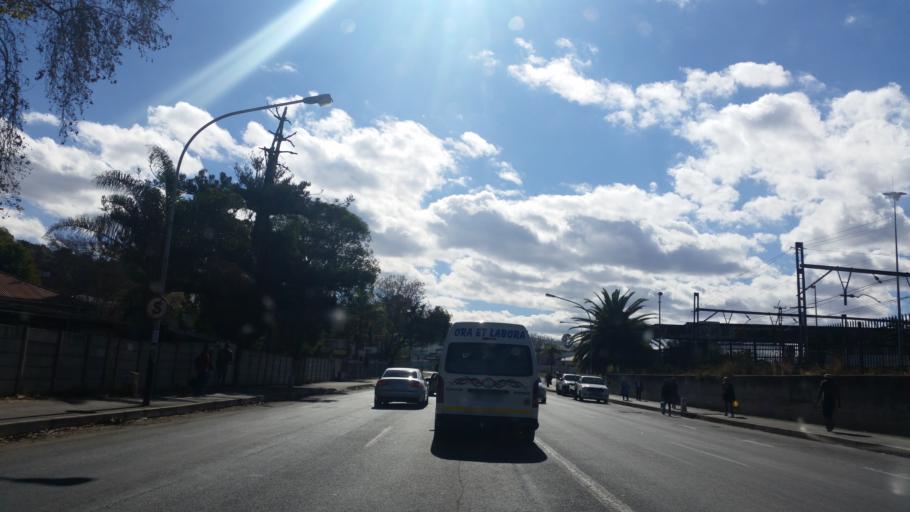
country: ZA
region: KwaZulu-Natal
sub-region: uThukela District Municipality
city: Ladysmith
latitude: -28.5569
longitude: 29.7851
